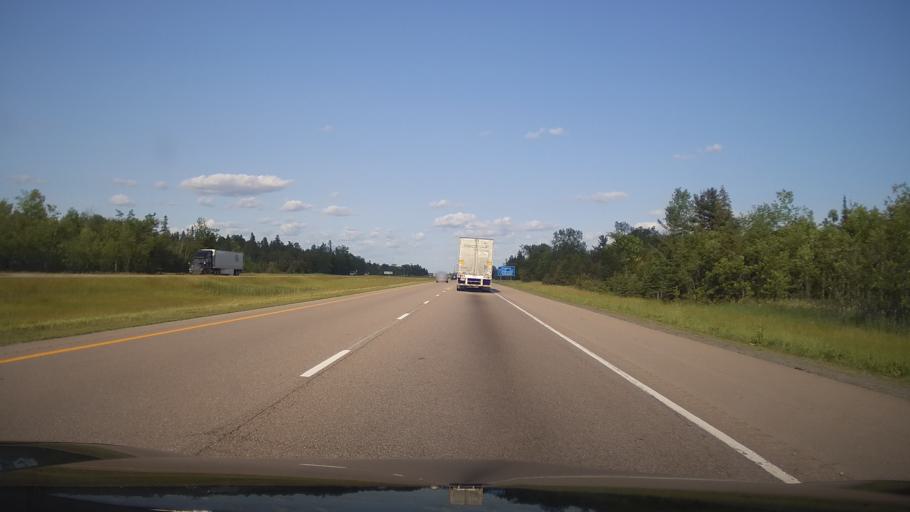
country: CA
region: Ontario
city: Kingston
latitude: 44.2846
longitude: -76.6740
